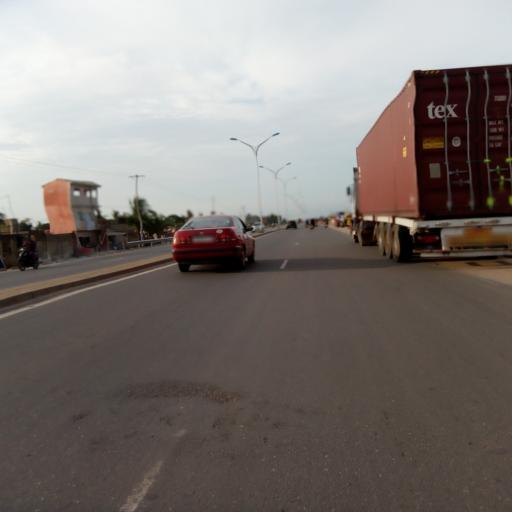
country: TG
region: Maritime
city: Lome
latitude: 6.1738
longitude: 1.2820
